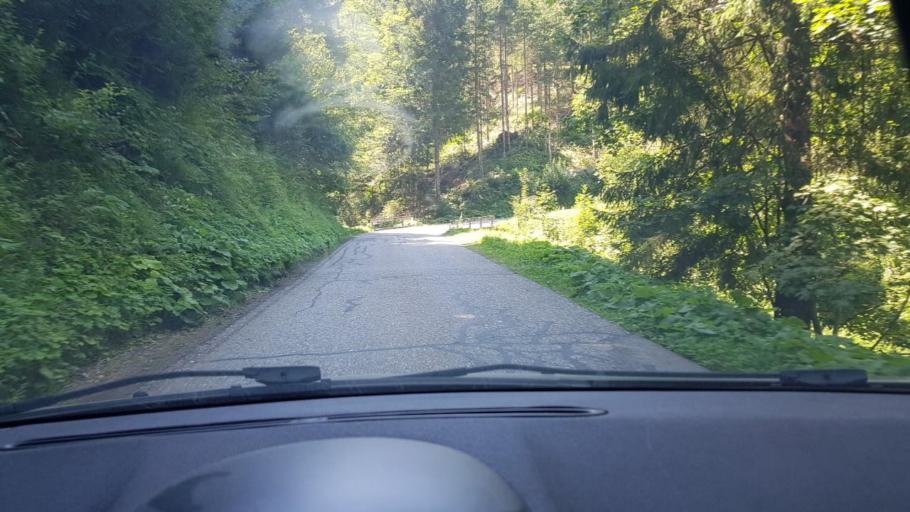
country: SI
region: Jezersko
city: Zgornje Jezersko
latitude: 46.4221
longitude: 14.5470
